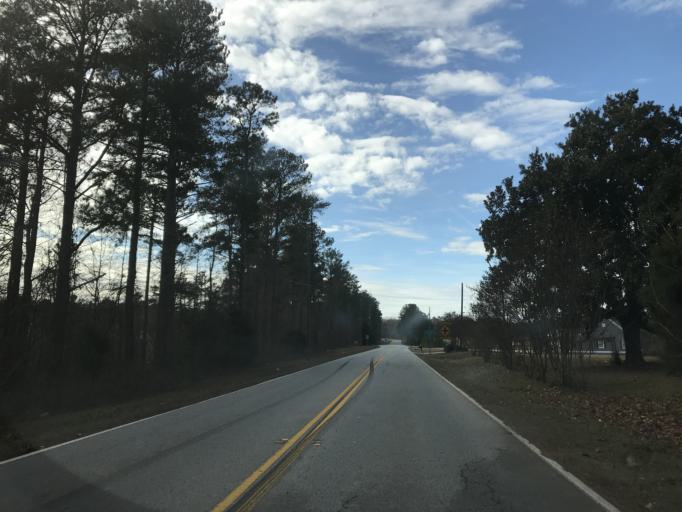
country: US
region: Georgia
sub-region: Douglas County
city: Douglasville
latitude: 33.7972
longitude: -84.7643
